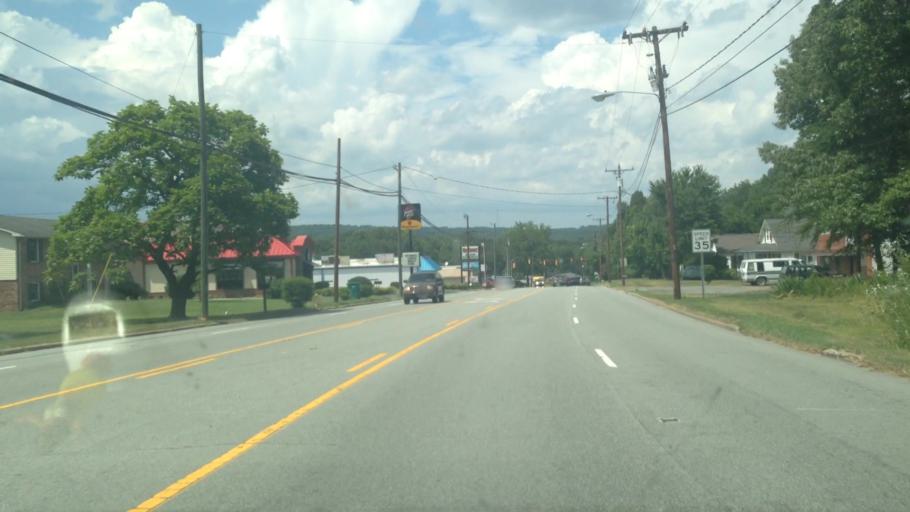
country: US
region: North Carolina
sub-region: Rockingham County
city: Mayodan
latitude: 36.3997
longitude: -79.9708
